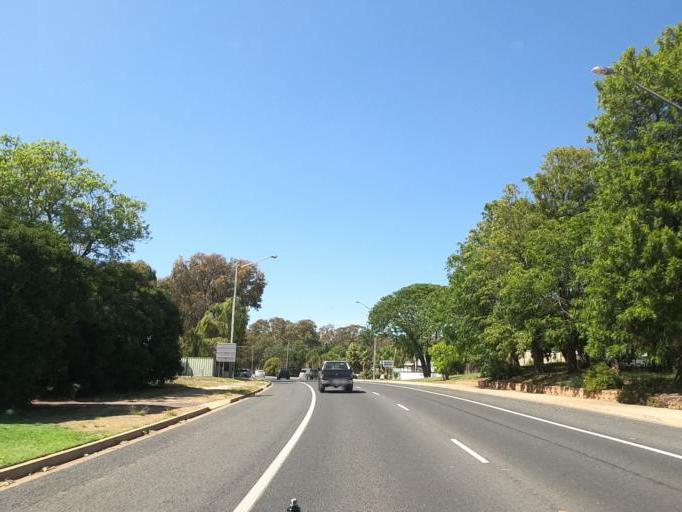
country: AU
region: New South Wales
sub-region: Corowa Shire
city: Mulwala
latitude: -35.9987
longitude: 146.0006
